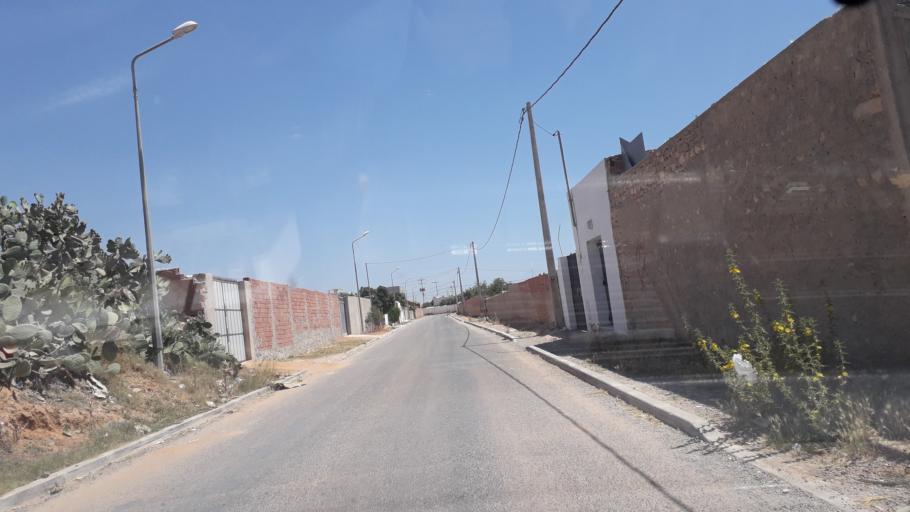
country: TN
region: Safaqis
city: Al Qarmadah
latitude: 34.8251
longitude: 10.7706
